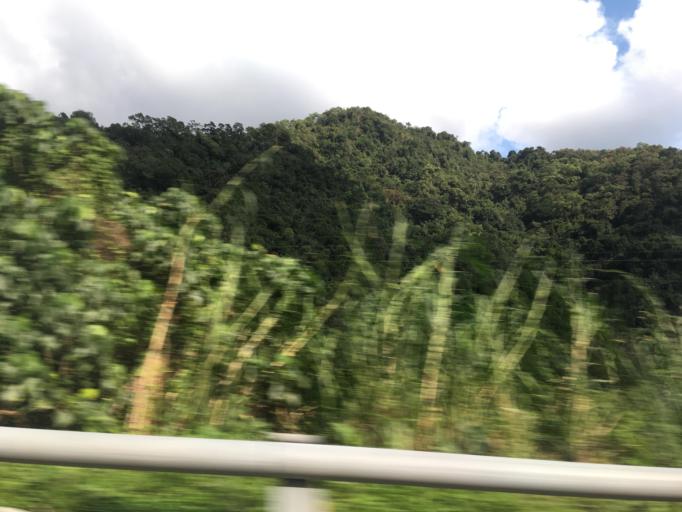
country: TW
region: Taiwan
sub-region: Yilan
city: Yilan
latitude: 24.7503
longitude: 121.6656
